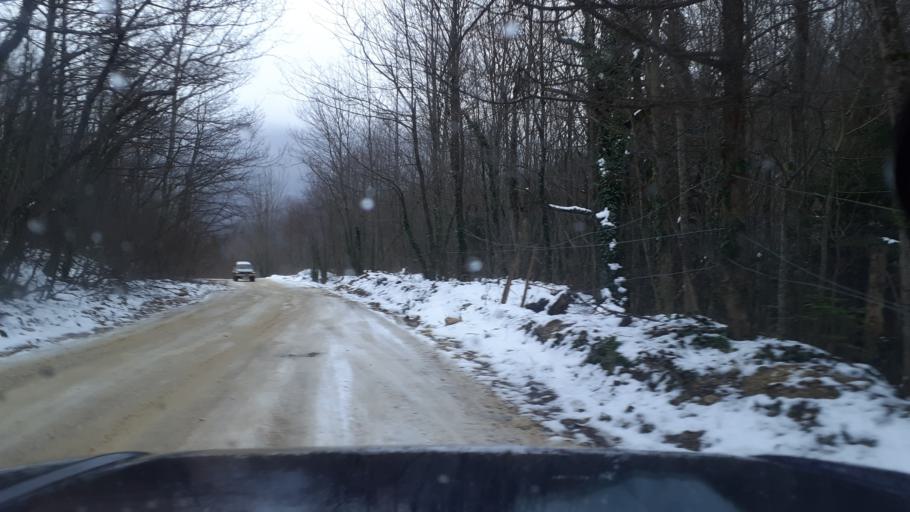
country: RU
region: Krasnodarskiy
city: Neftegorsk
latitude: 44.1257
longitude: 39.8035
